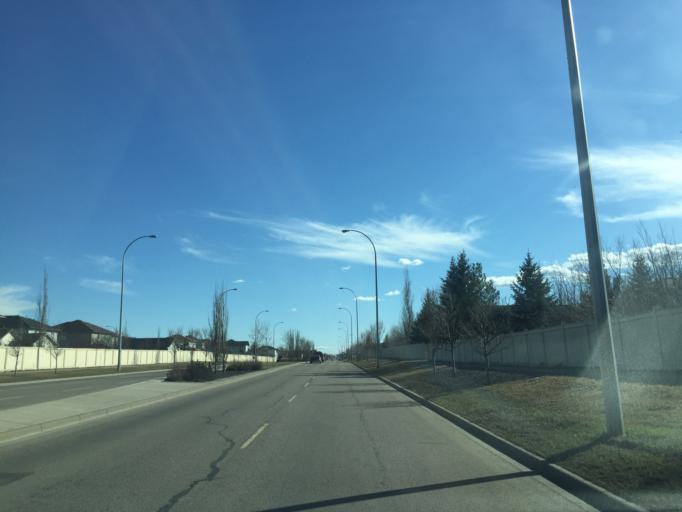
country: CA
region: Alberta
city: Airdrie
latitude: 51.2981
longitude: -114.0254
